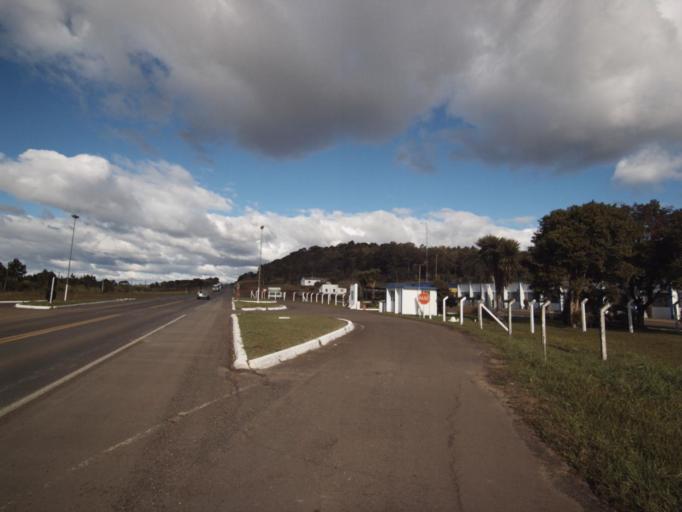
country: BR
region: Santa Catarina
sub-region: Joacaba
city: Joacaba
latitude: -27.1732
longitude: -51.5537
